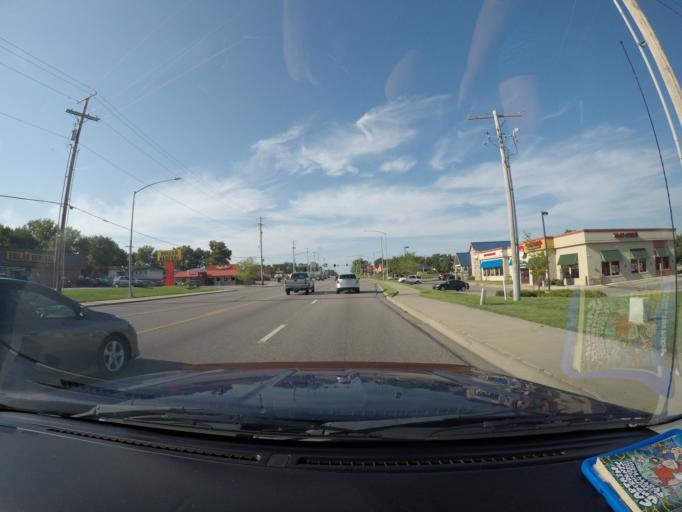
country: US
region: Kansas
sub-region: Leavenworth County
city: Lansing
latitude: 39.2562
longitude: -94.8999
